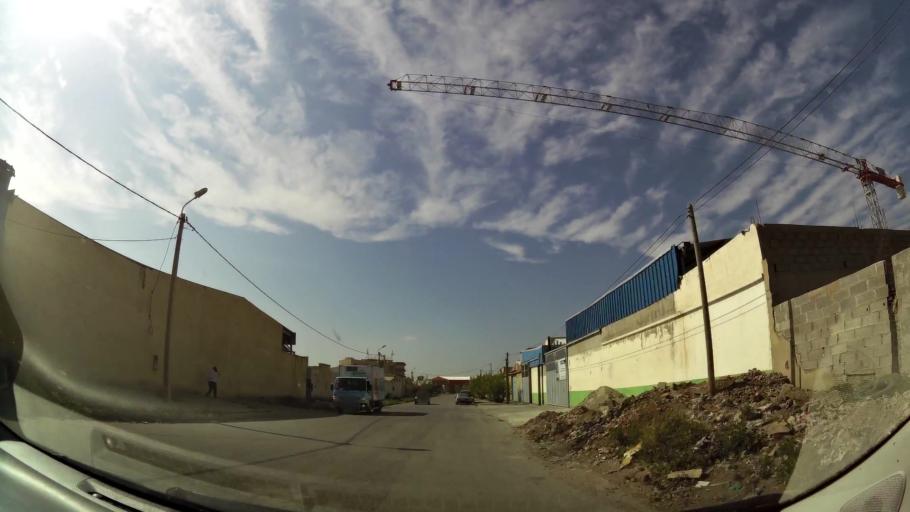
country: MA
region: Oriental
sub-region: Oujda-Angad
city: Oujda
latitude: 34.7034
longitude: -1.8860
